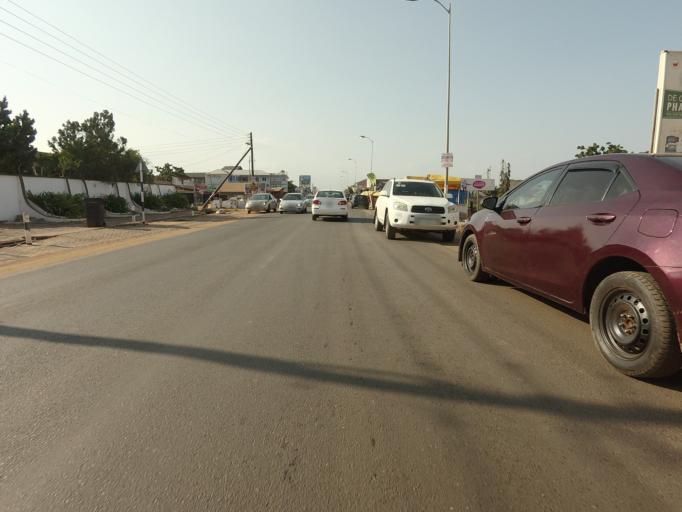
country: GH
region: Greater Accra
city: Nungua
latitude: 5.6358
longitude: -0.0762
